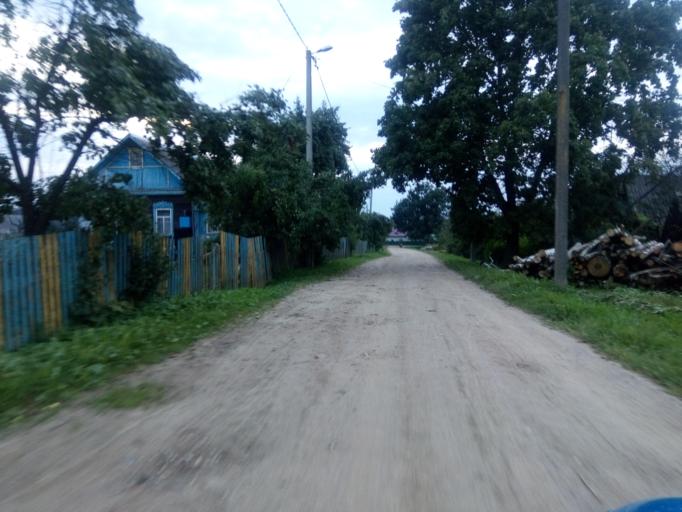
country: BY
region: Vitebsk
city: Dzisna
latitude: 55.6697
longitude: 28.3214
